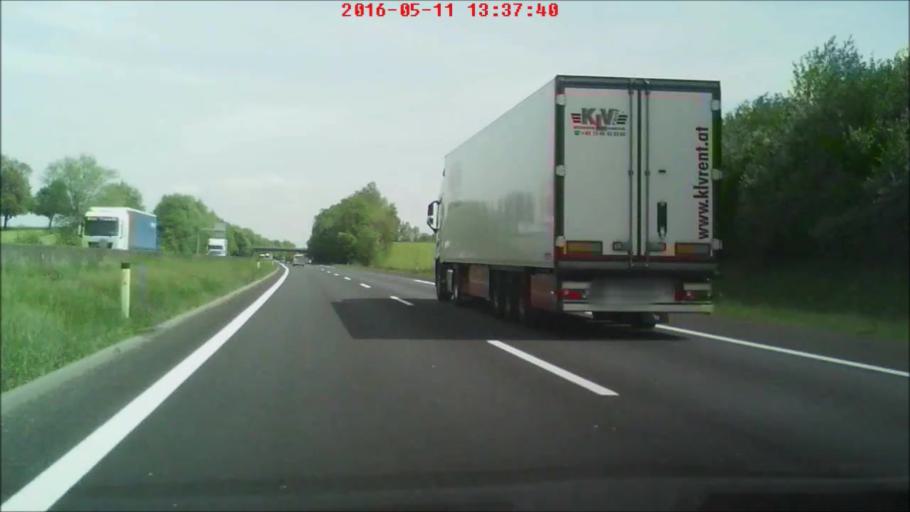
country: AT
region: Upper Austria
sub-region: Politischer Bezirk Ried im Innkreis
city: Ried im Innkreis
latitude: 48.2660
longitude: 13.5012
